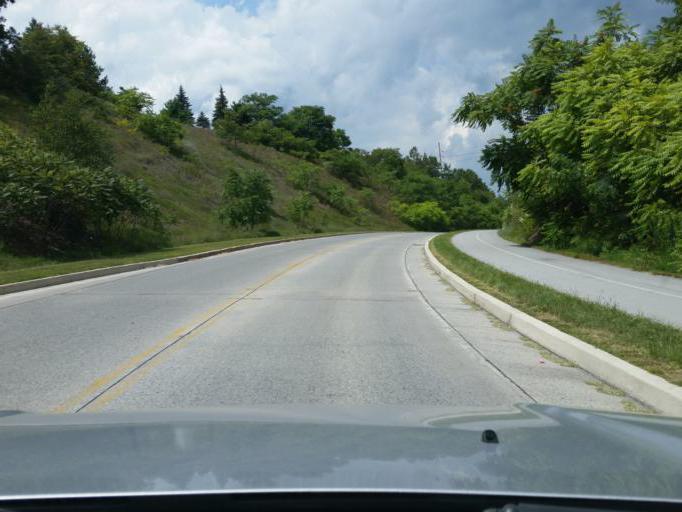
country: US
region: Pennsylvania
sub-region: Blair County
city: Altoona
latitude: 40.5298
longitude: -78.3895
